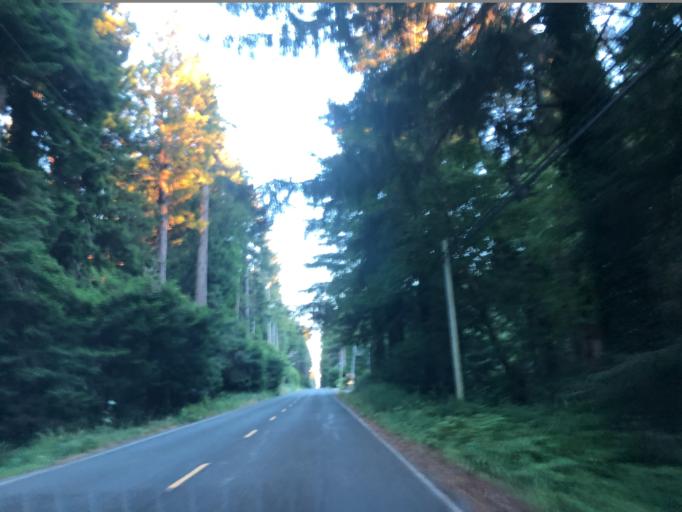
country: US
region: California
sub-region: Humboldt County
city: Westhaven-Moonstone
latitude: 41.0822
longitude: -124.1479
